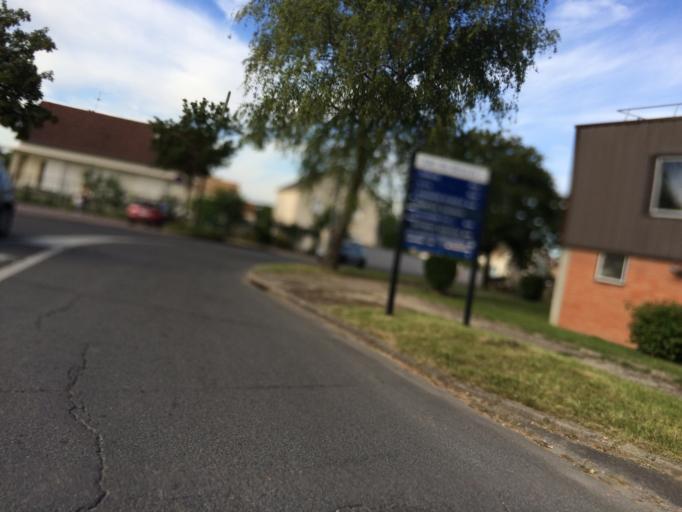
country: FR
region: Ile-de-France
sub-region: Departement de l'Essonne
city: Saulx-les-Chartreux
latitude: 48.6934
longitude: 2.2723
